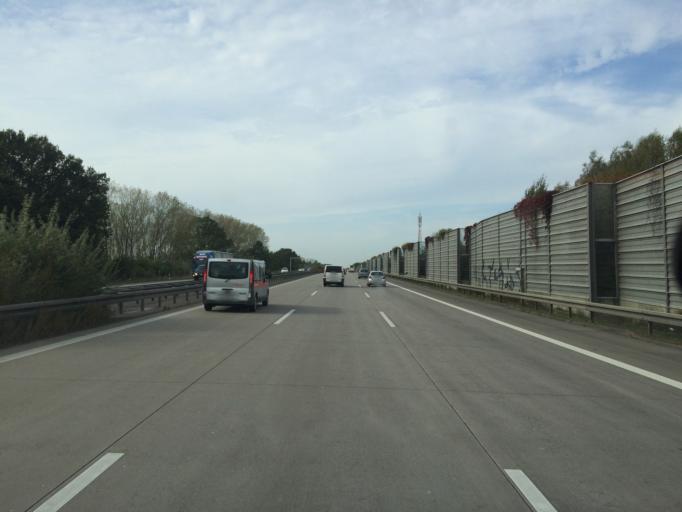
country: DE
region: Saxony-Anhalt
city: Schermen
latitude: 52.2265
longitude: 11.8129
